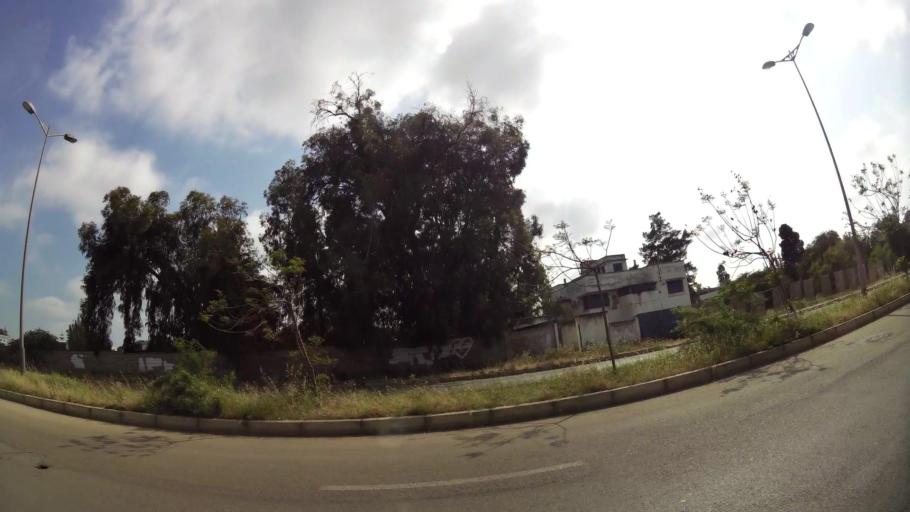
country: MA
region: Rabat-Sale-Zemmour-Zaer
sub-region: Rabat
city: Rabat
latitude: 33.9714
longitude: -6.8519
